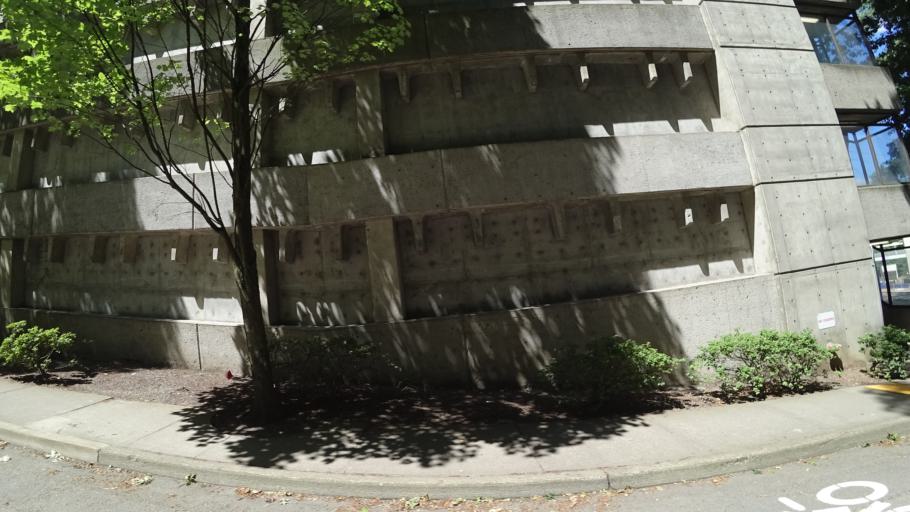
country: US
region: Oregon
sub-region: Multnomah County
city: Portland
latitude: 45.4981
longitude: -122.6849
